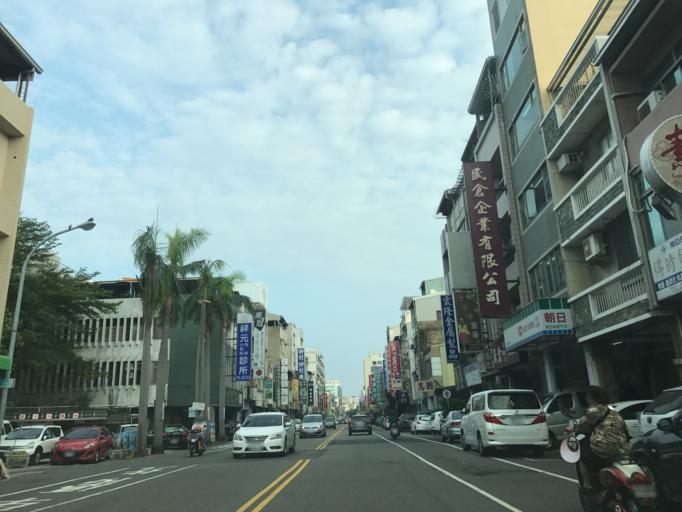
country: TW
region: Taiwan
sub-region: Tainan
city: Tainan
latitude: 23.0000
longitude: 120.1927
